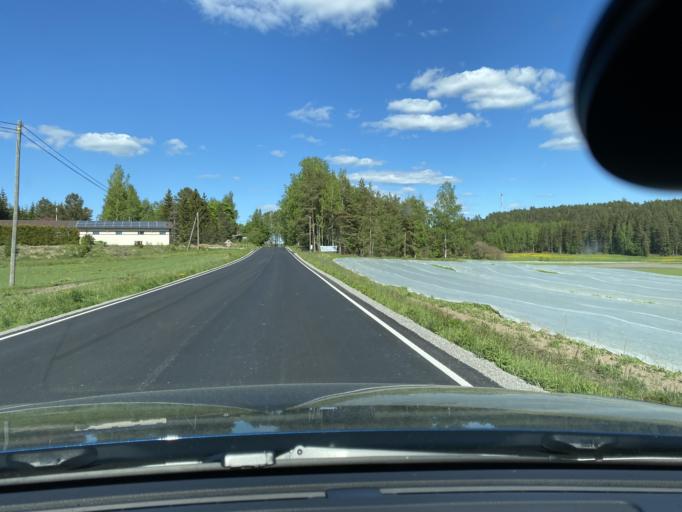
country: FI
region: Varsinais-Suomi
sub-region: Turku
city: Sauvo
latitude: 60.3339
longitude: 22.6833
